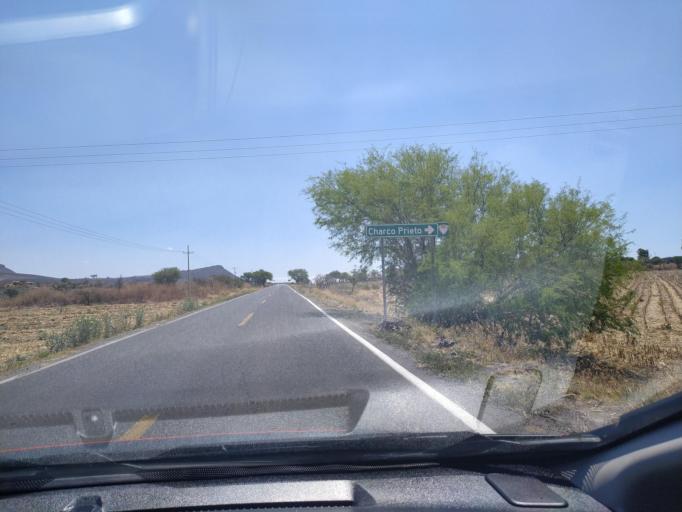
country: MX
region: Guanajuato
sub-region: San Francisco del Rincon
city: San Ignacio de Hidalgo
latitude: 20.8270
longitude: -101.8432
